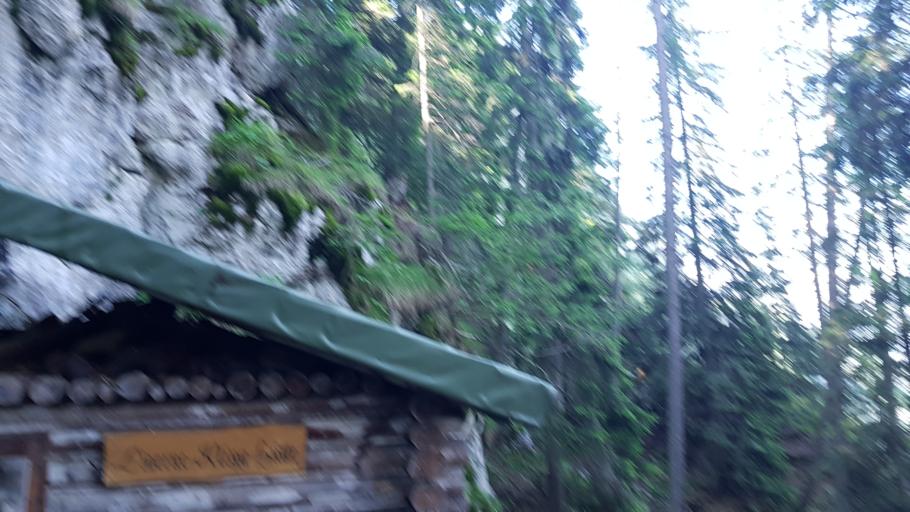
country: AT
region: Styria
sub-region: Politischer Bezirk Graz-Umgebung
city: Rothelstein
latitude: 47.3654
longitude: 15.4230
